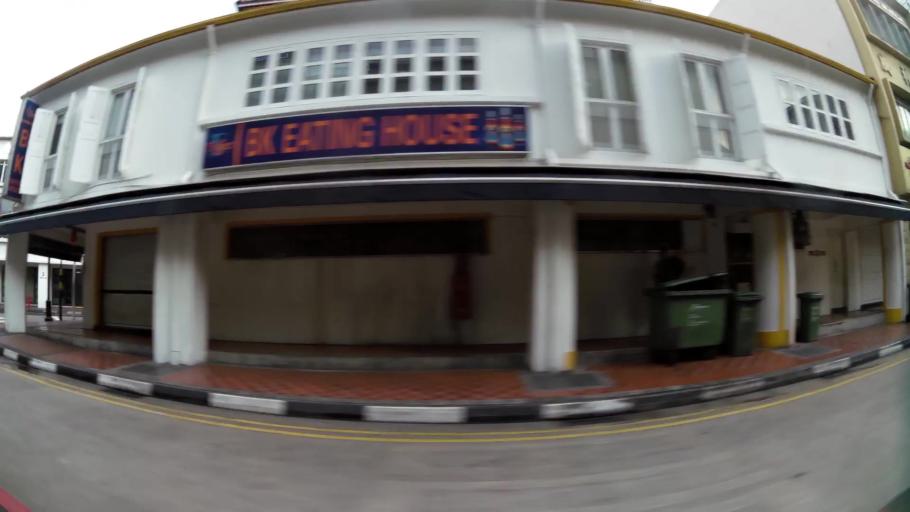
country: SG
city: Singapore
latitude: 1.2878
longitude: 103.8486
